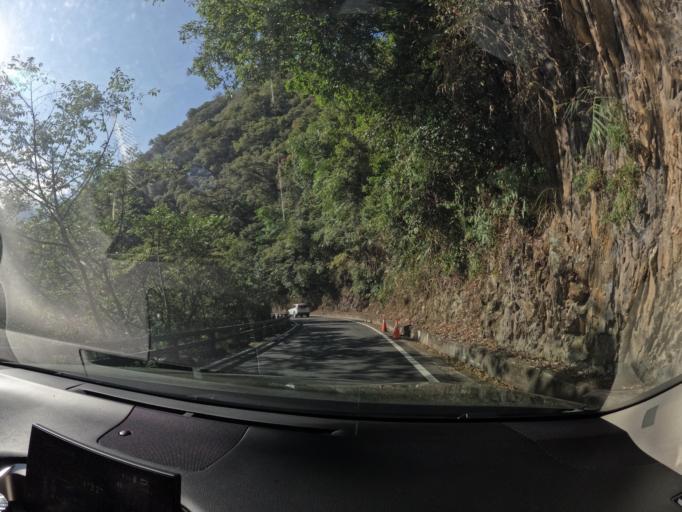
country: TW
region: Taiwan
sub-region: Taitung
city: Taitung
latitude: 23.1772
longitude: 121.0428
